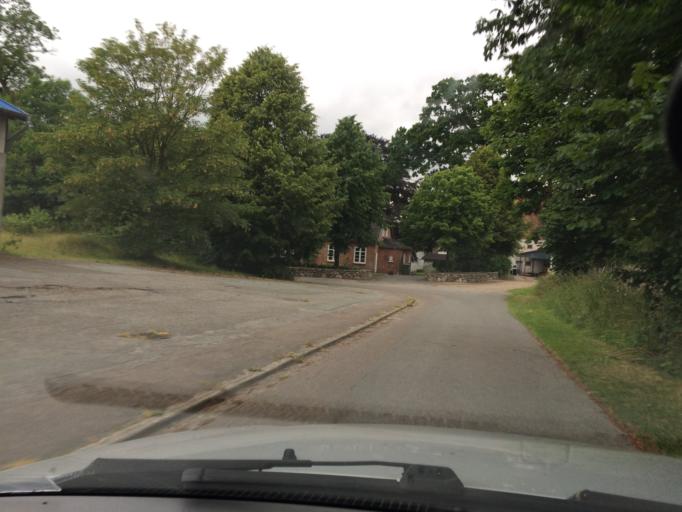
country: DE
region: Schleswig-Holstein
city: Oeversee
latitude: 54.6934
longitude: 9.4304
